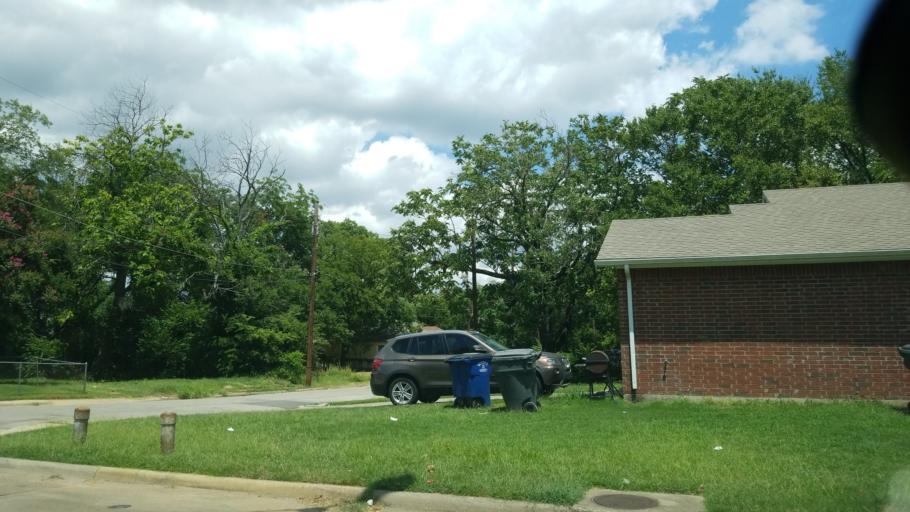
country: US
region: Texas
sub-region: Dallas County
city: Dallas
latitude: 32.7521
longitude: -96.7527
